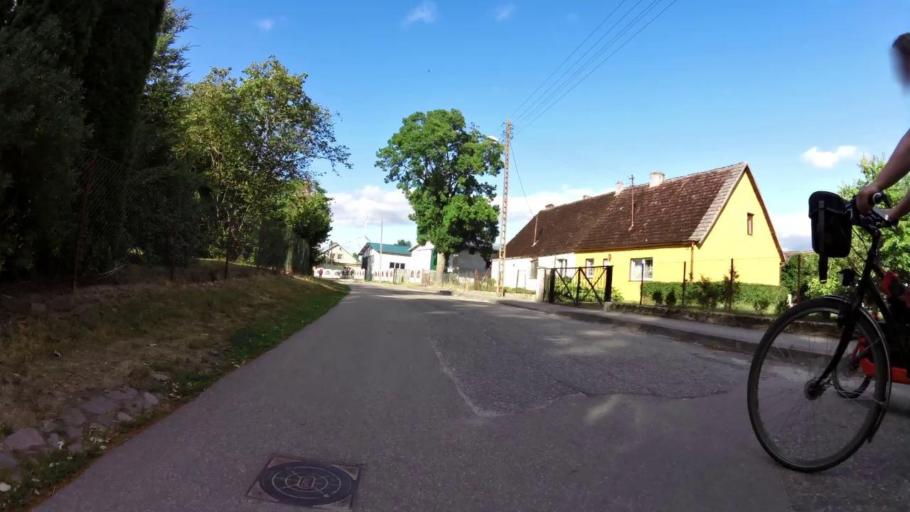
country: PL
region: West Pomeranian Voivodeship
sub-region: Powiat swidwinski
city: Swidwin
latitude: 53.6846
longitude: 15.7440
